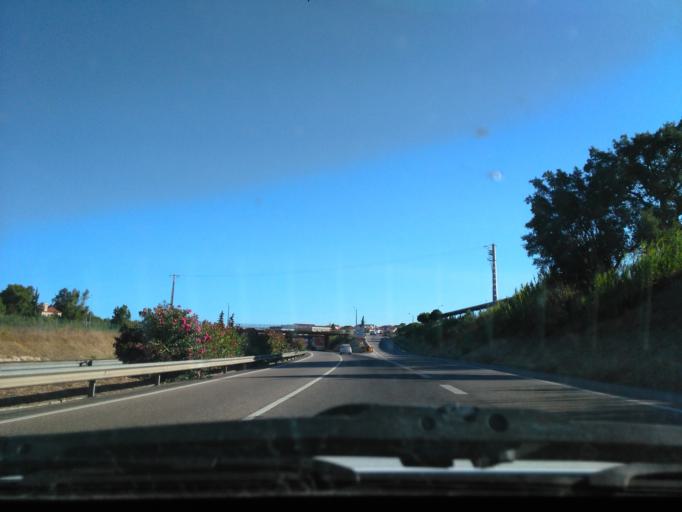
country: PT
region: Santarem
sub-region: Santarem
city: Santarem
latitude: 39.2458
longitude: -8.6954
